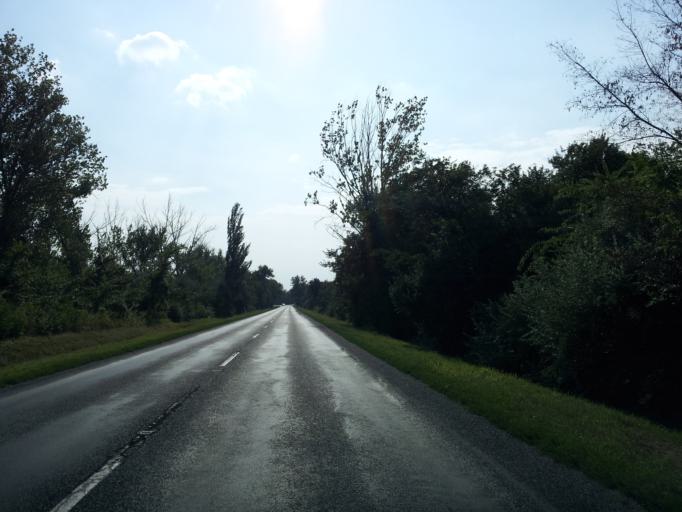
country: HU
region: Somogy
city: Balatonszabadi
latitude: 46.9368
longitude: 18.1492
